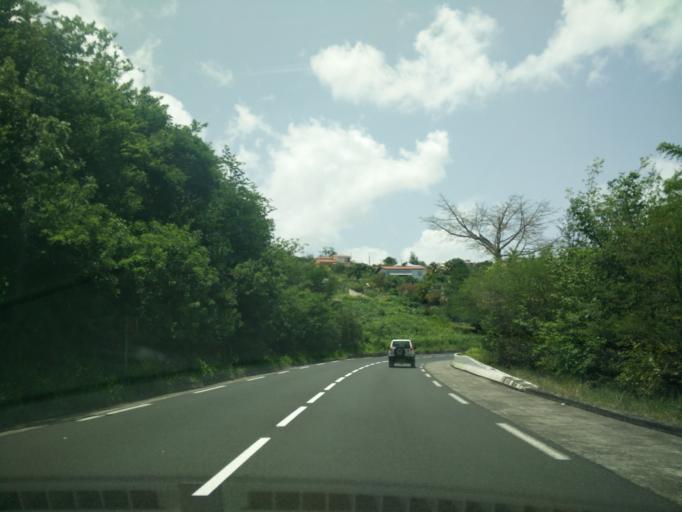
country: MQ
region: Martinique
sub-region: Martinique
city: Fort-de-France
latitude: 14.6337
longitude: -61.1270
